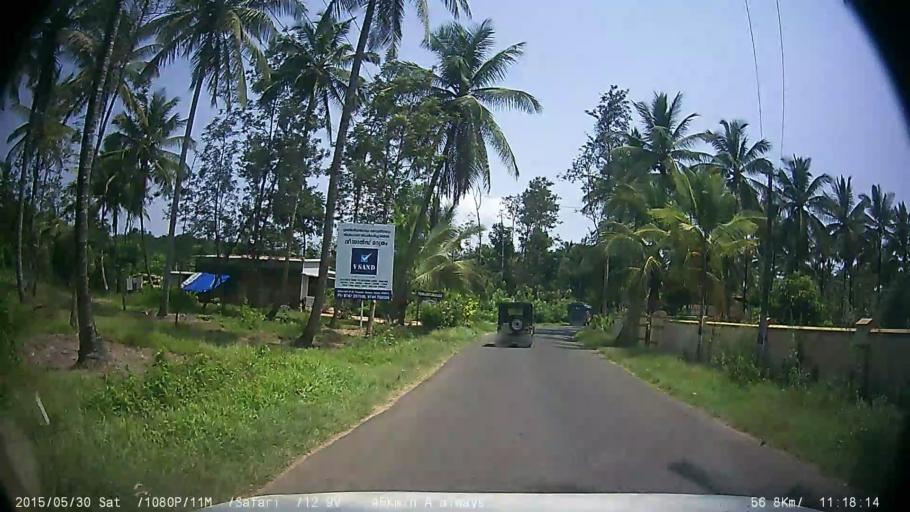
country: IN
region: Kerala
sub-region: Wayanad
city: Panamaram
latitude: 11.7832
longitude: 76.0458
